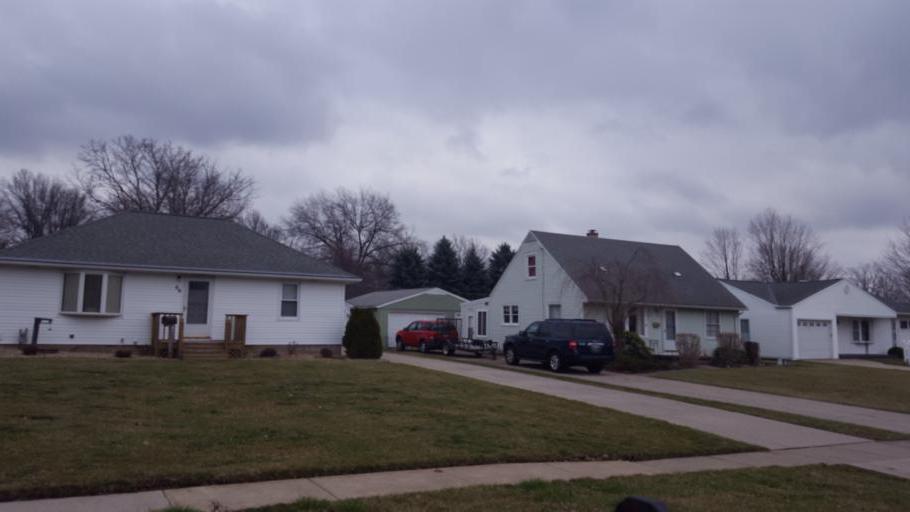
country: US
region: Ohio
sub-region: Richland County
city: Shelby
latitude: 40.8767
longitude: -82.6461
